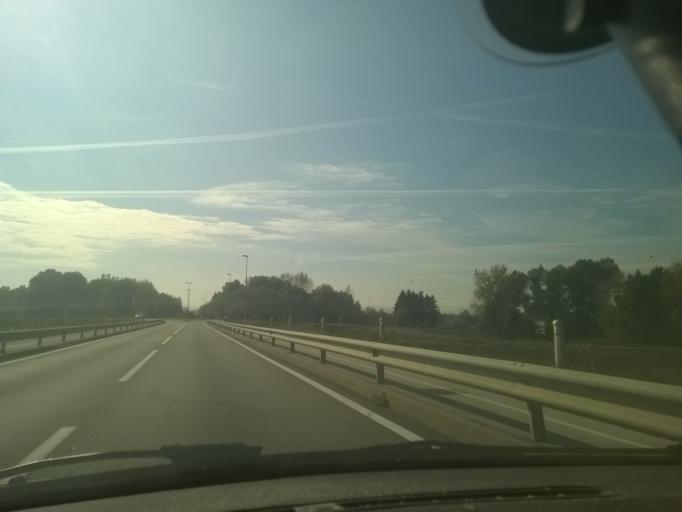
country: SI
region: Ptuj
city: Ptuj
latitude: 46.4084
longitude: 15.8770
